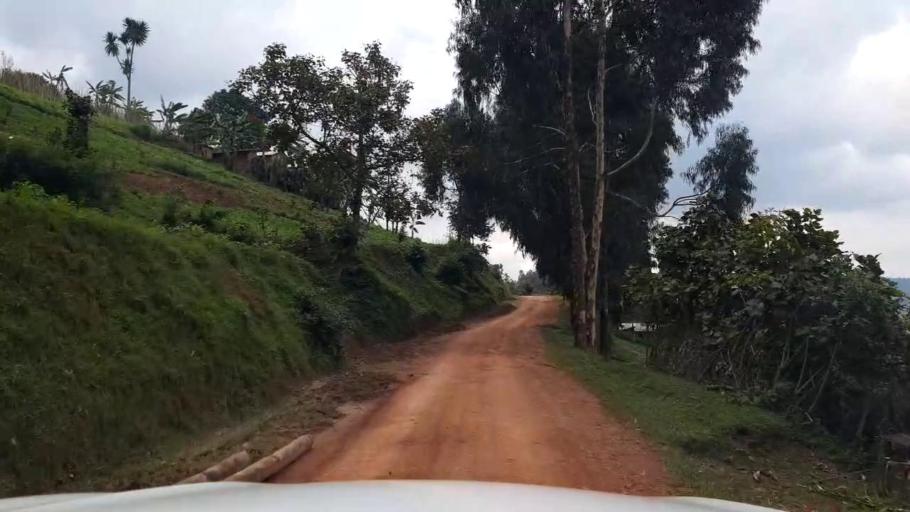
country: UG
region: Western Region
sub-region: Kabale District
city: Kabale
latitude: -1.4267
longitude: 29.8684
